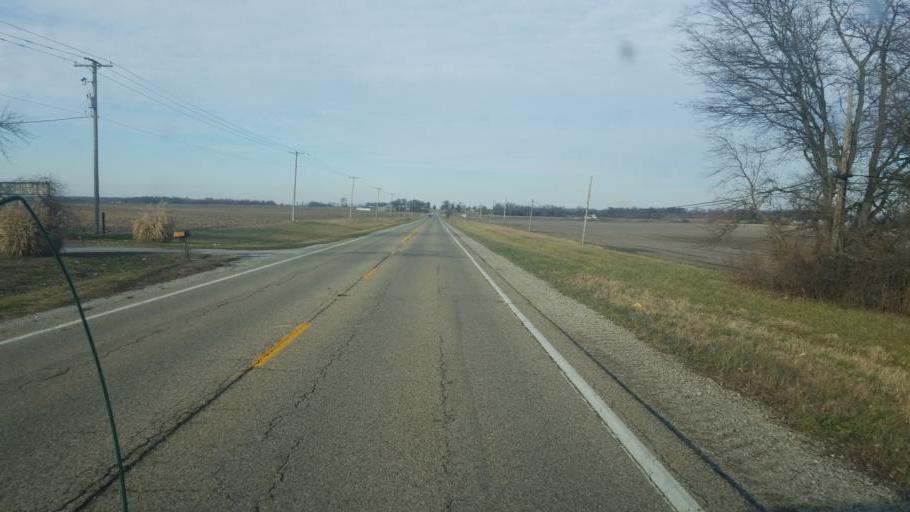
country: US
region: Illinois
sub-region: Lawrence County
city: Bridgeport
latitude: 38.5987
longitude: -87.6943
